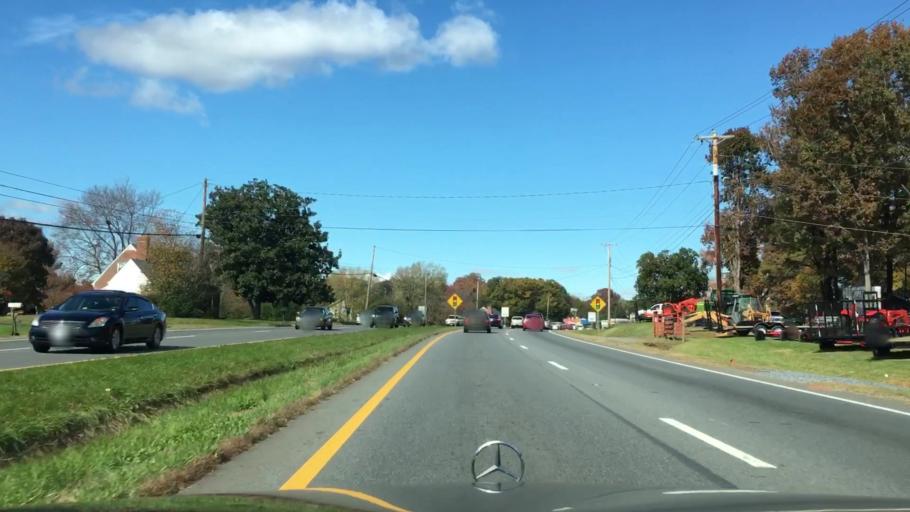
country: US
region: Virginia
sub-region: Campbell County
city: Timberlake
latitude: 37.3156
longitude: -79.1872
